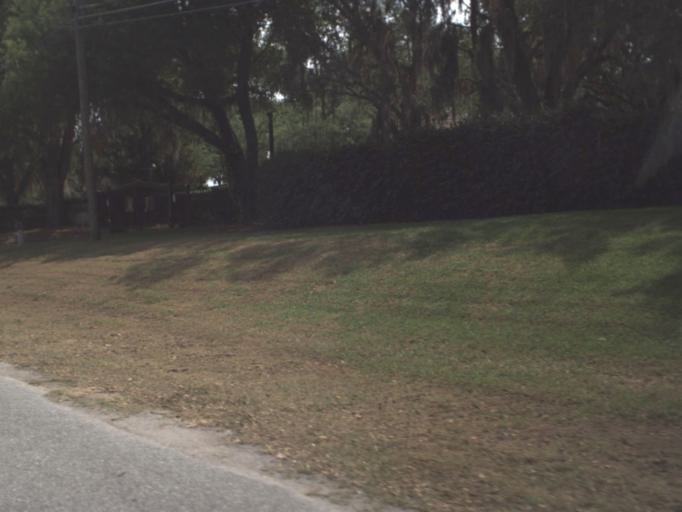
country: US
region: Florida
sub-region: Lake County
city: Howie In The Hills
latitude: 28.7219
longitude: -81.7756
